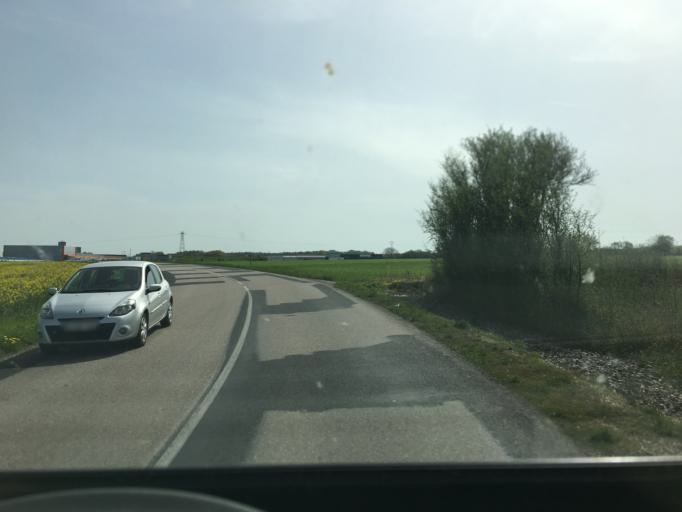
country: FR
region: Lorraine
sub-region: Departement de Meurthe-et-Moselle
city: Art-sur-Meurthe
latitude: 48.6151
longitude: 6.2602
